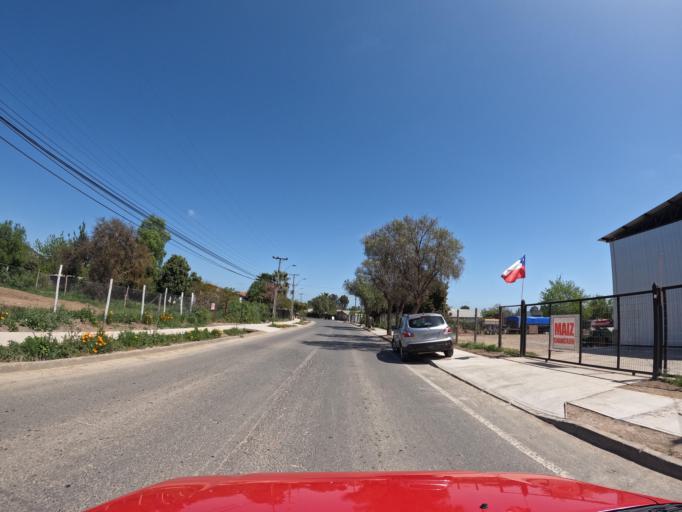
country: CL
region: O'Higgins
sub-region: Provincia de Colchagua
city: Santa Cruz
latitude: -34.7275
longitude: -71.6603
